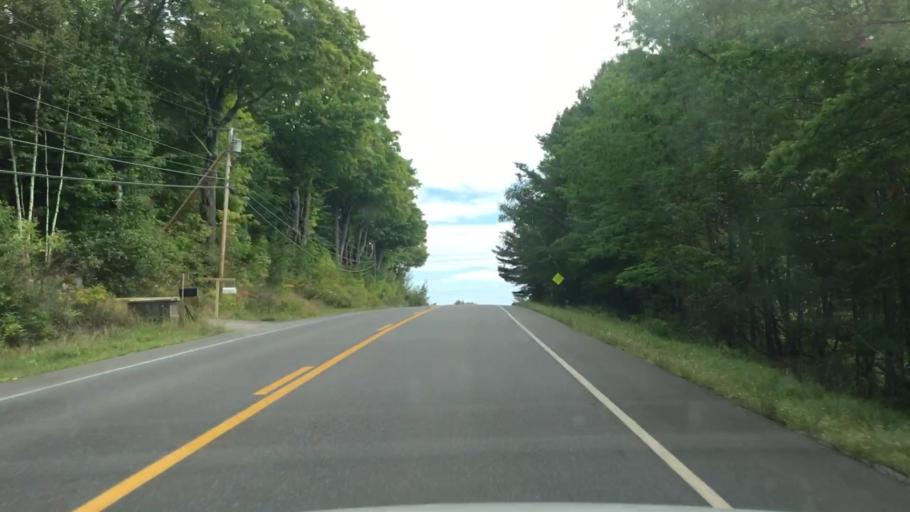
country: US
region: Maine
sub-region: Piscataquis County
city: Dover-Foxcroft
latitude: 45.2246
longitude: -69.1260
